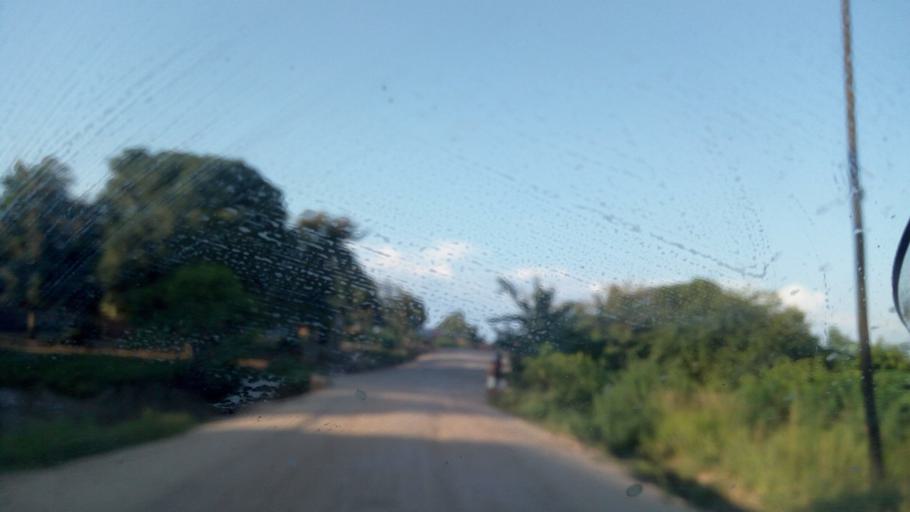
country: BI
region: Bururi
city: Rumonge
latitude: -4.1206
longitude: 29.0841
